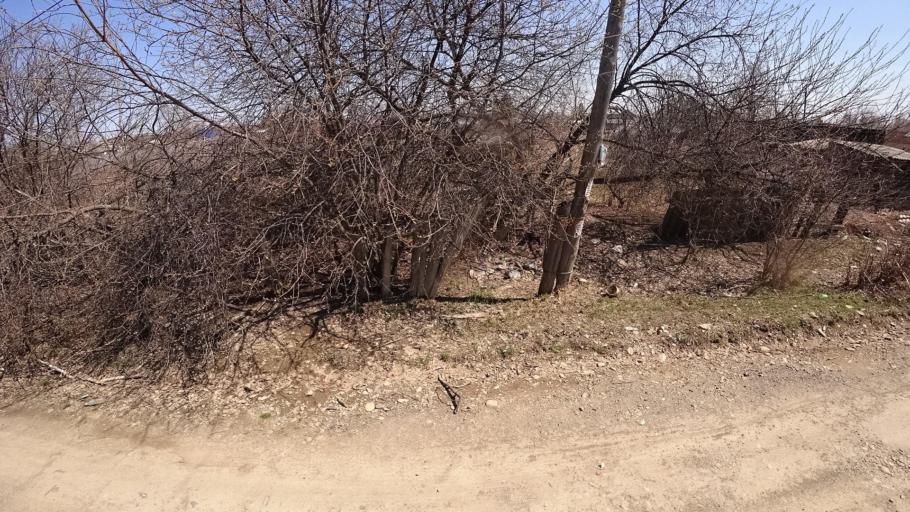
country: RU
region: Khabarovsk Krai
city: Khurba
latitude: 50.4119
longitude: 136.8623
